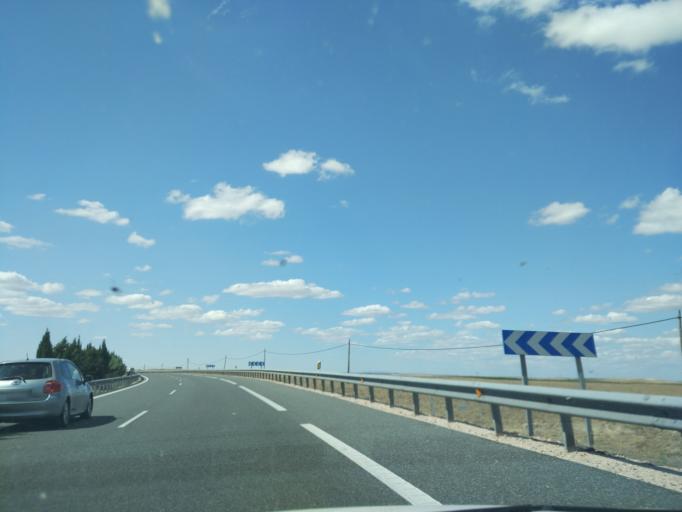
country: ES
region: Castille and Leon
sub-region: Provincia de Valladolid
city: Ataquines
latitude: 41.1893
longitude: -4.8115
